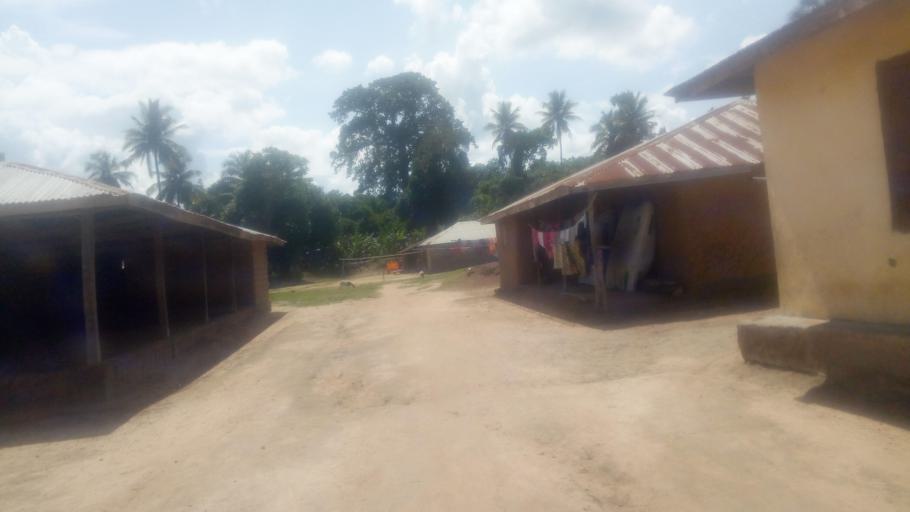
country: SL
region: Northern Province
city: Magburaka
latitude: 8.6512
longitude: -12.0691
